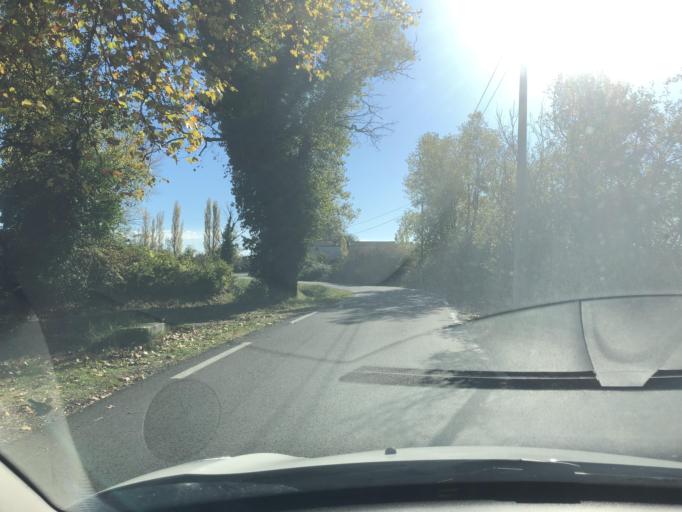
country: FR
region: Provence-Alpes-Cote d'Azur
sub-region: Departement du Vaucluse
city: Entraigues-sur-la-Sorgue
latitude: 43.9862
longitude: 4.9384
